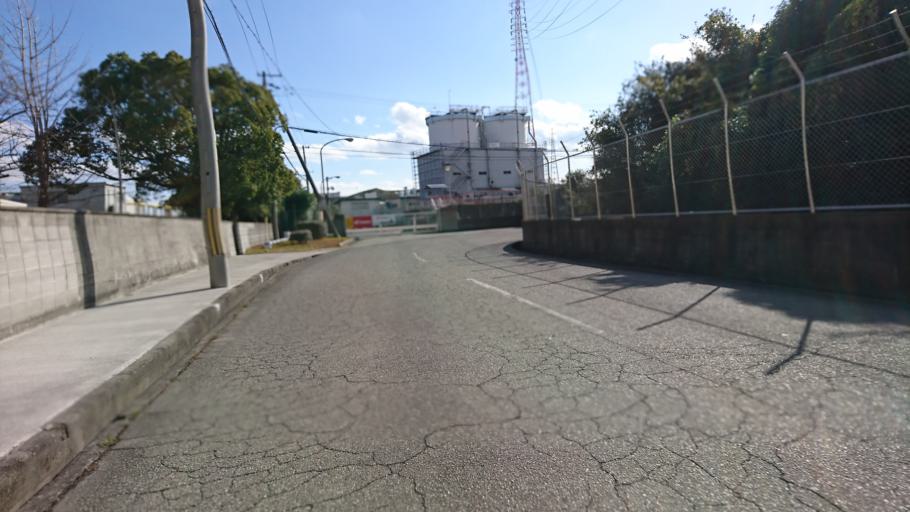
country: JP
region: Hyogo
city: Shirahamacho-usazakiminami
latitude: 34.7568
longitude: 134.7665
